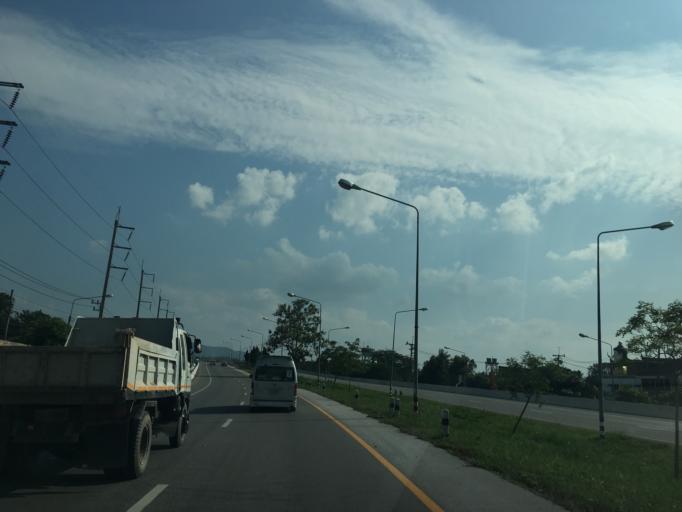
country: TH
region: Chiang Rai
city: Mae Lao
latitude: 19.7180
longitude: 99.7162
